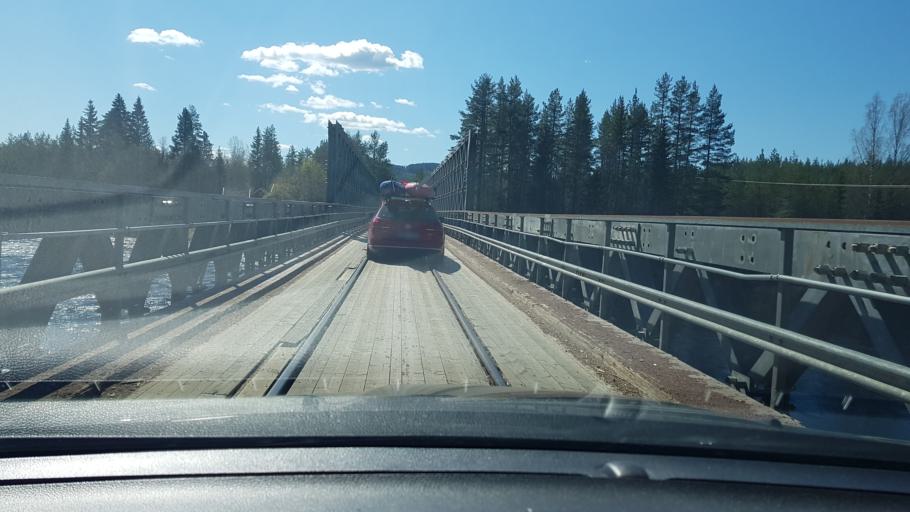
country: SE
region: Dalarna
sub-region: Alvdalens Kommun
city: AElvdalen
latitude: 61.1332
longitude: 14.1716
